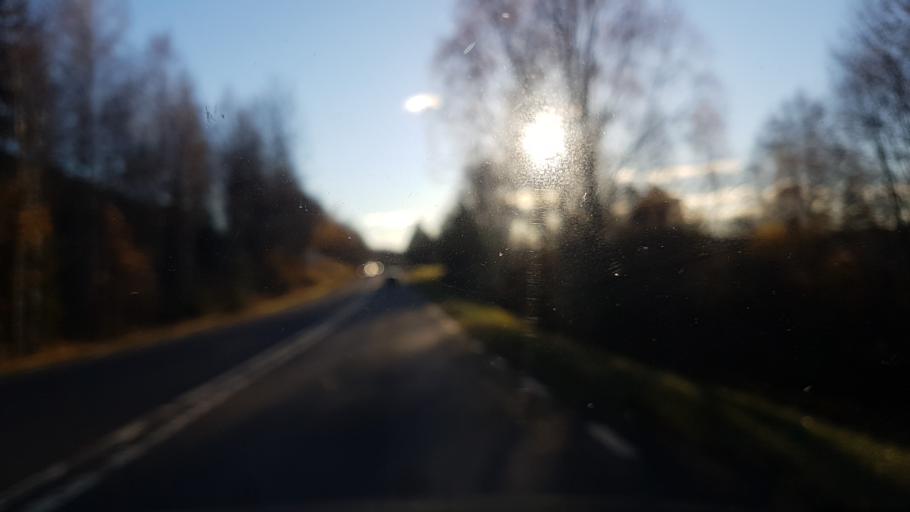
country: SE
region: Gaevleborg
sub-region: Hofors Kommun
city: Hofors
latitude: 60.5524
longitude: 16.3148
